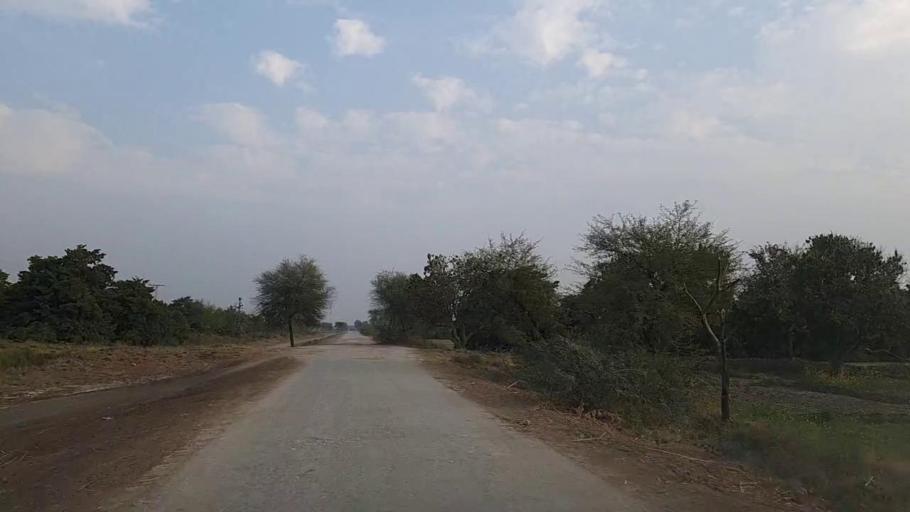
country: PK
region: Sindh
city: Mirwah Gorchani
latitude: 25.3005
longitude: 69.2205
